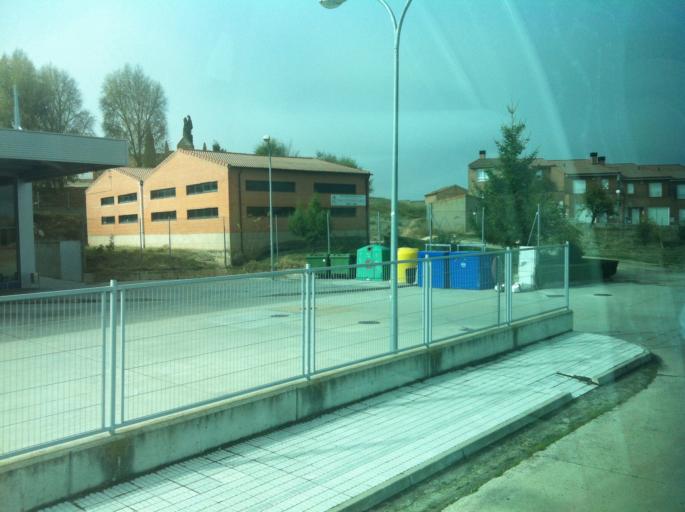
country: ES
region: Castille and Leon
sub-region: Provincia de Burgos
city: Lerma
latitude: 42.0252
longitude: -3.7645
